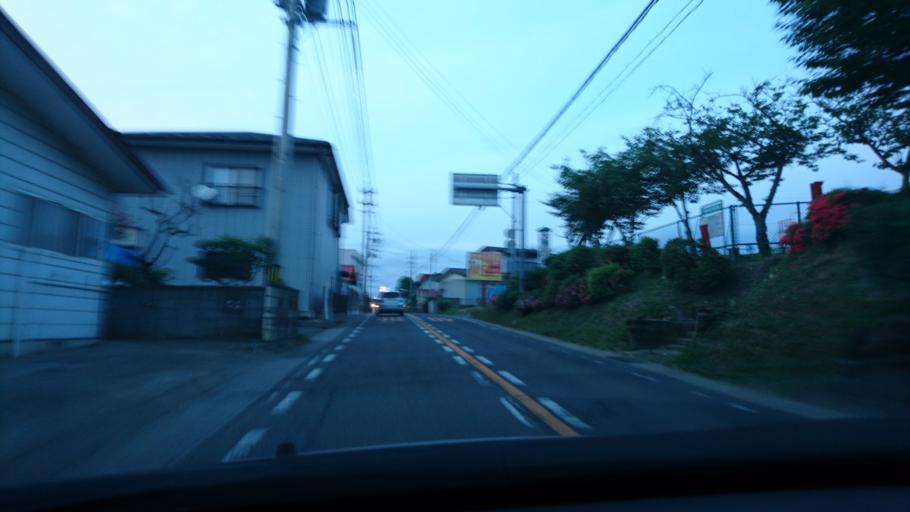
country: JP
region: Iwate
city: Ichinoseki
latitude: 38.8146
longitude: 140.9854
